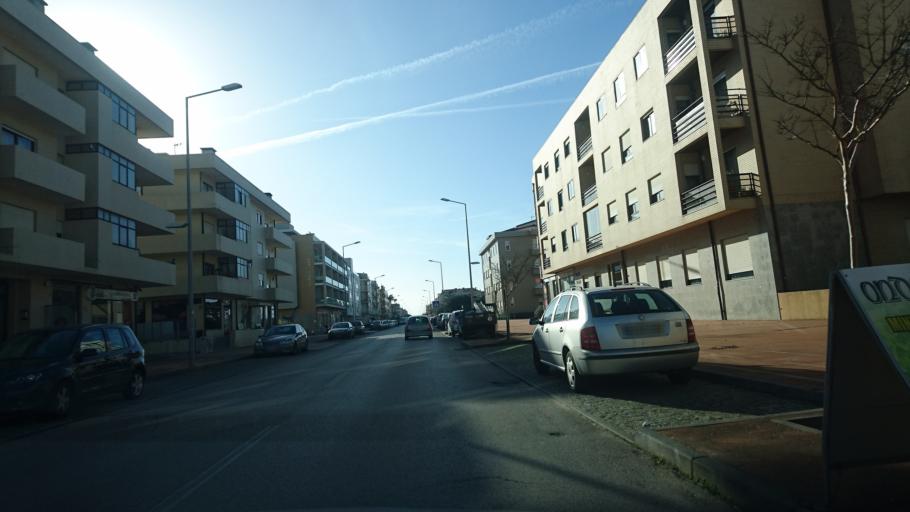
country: PT
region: Aveiro
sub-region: Ovar
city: Esmoriz
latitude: 40.9546
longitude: -8.6417
